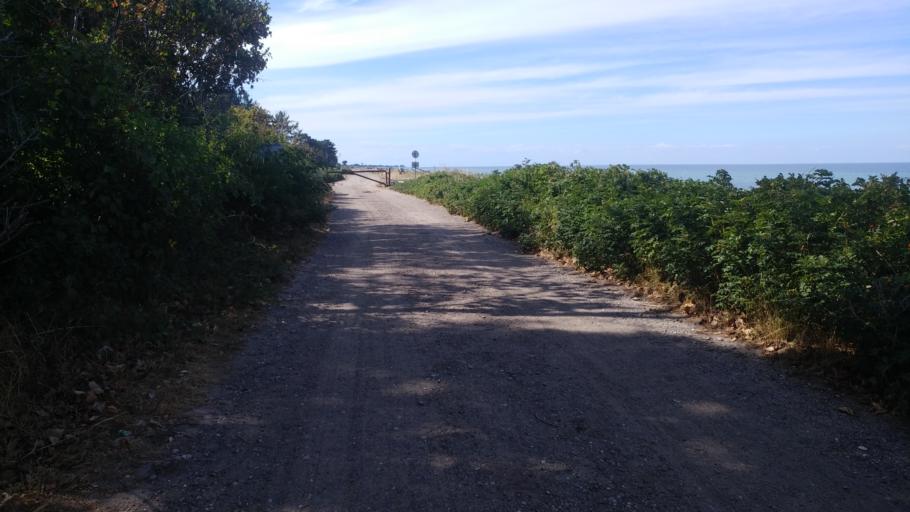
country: DK
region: South Denmark
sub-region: Kerteminde Kommune
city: Munkebo
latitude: 55.5485
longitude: 10.4993
